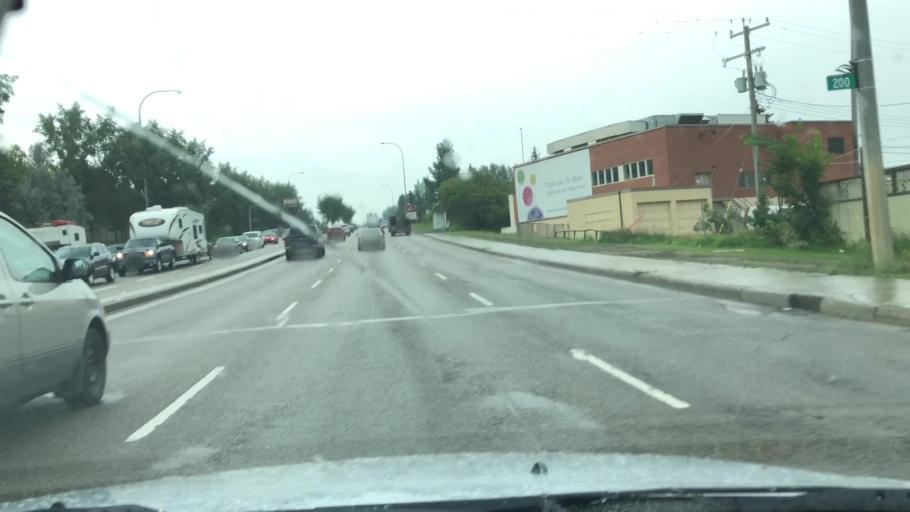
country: CA
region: Alberta
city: St. Albert
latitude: 53.6354
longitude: -113.6235
